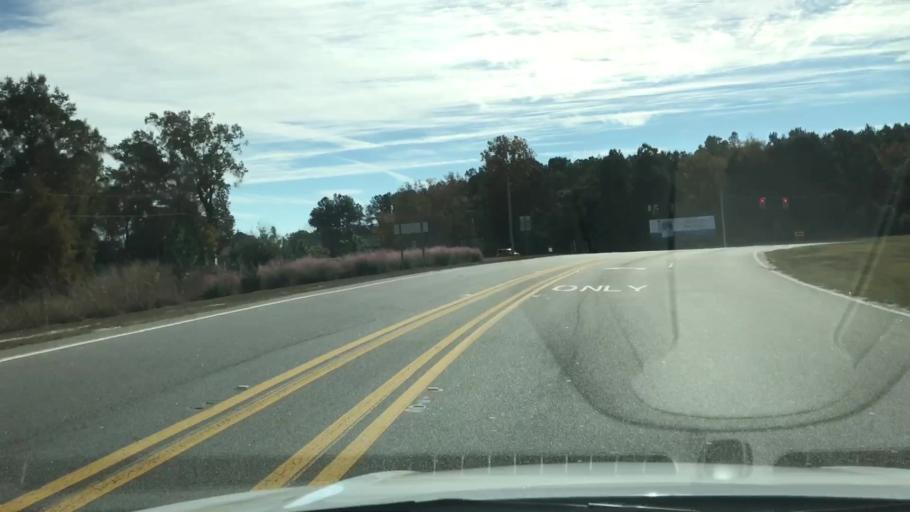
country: US
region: South Carolina
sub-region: Charleston County
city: Ravenel
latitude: 32.7747
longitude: -80.4613
